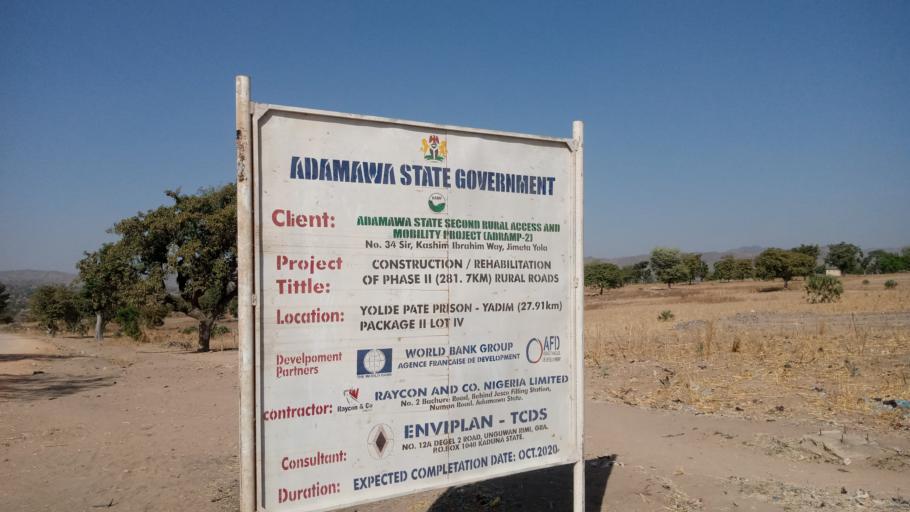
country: NG
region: Adamawa
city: Yola
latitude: 8.9741
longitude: 12.4044
